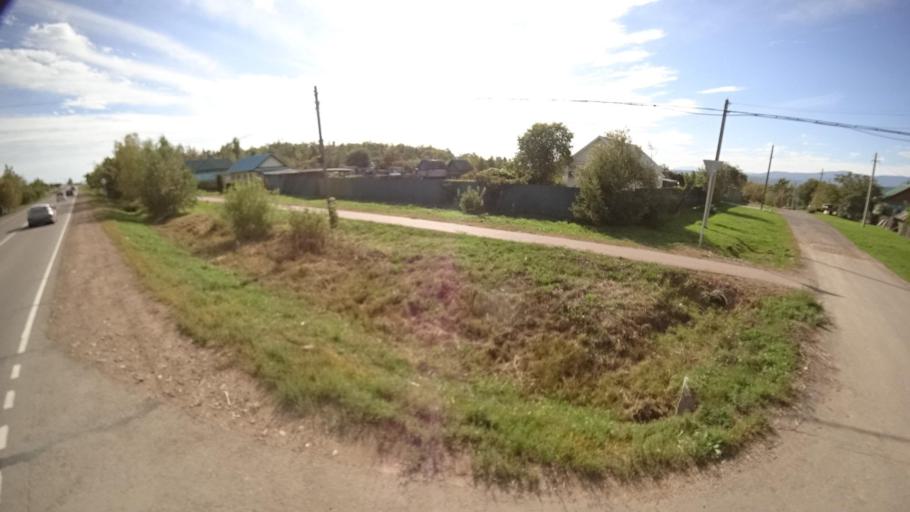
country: RU
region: Primorskiy
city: Dostoyevka
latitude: 44.3054
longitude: 133.4503
